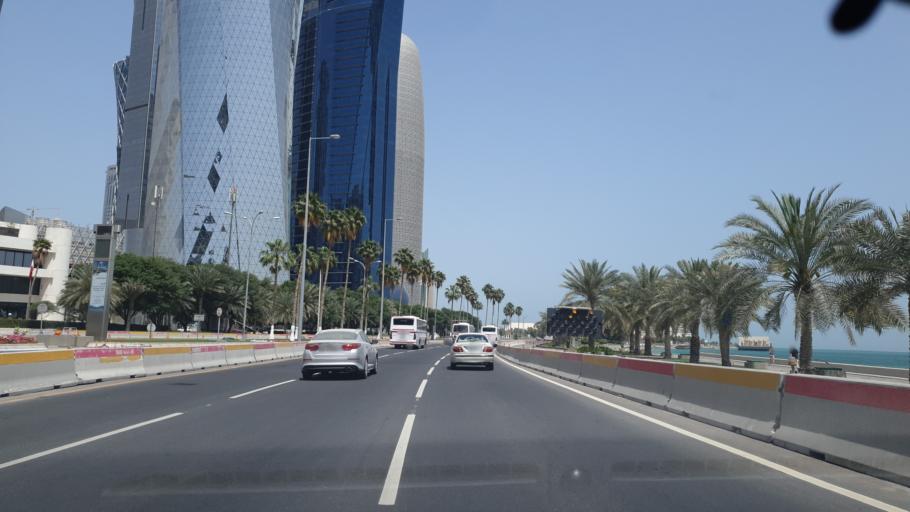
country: QA
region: Baladiyat ad Dawhah
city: Doha
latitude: 25.3148
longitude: 51.5248
